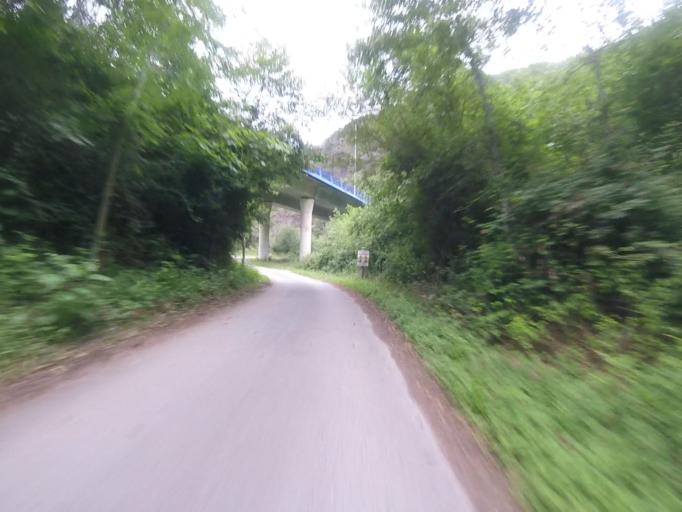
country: ES
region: Navarre
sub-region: Provincia de Navarra
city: Igantzi
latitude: 43.2177
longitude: -1.6720
